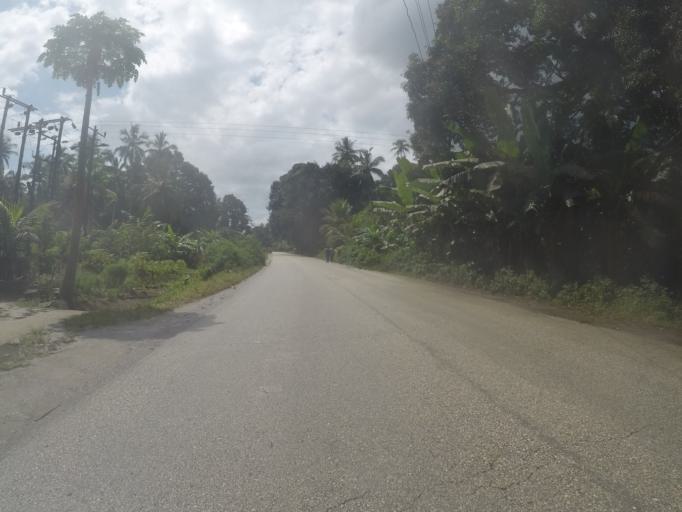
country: TZ
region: Zanzibar North
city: Gamba
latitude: -5.9844
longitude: 39.2513
